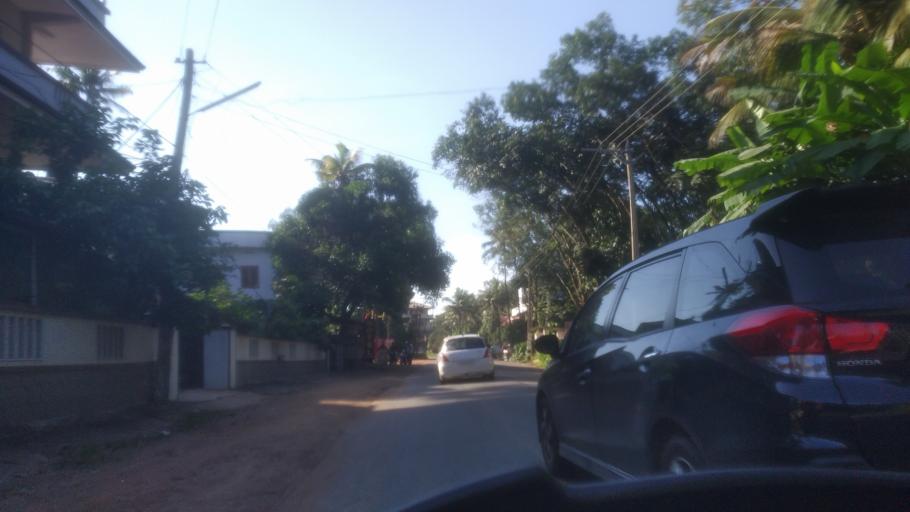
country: IN
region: Kerala
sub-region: Ernakulam
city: Ramamangalam
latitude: 9.9780
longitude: 76.4897
